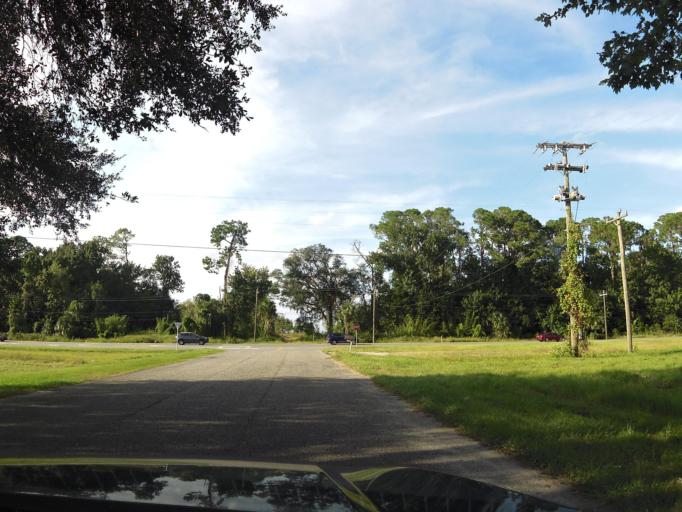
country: US
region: Florida
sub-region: Clay County
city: Green Cove Springs
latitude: 29.9833
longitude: -81.6715
